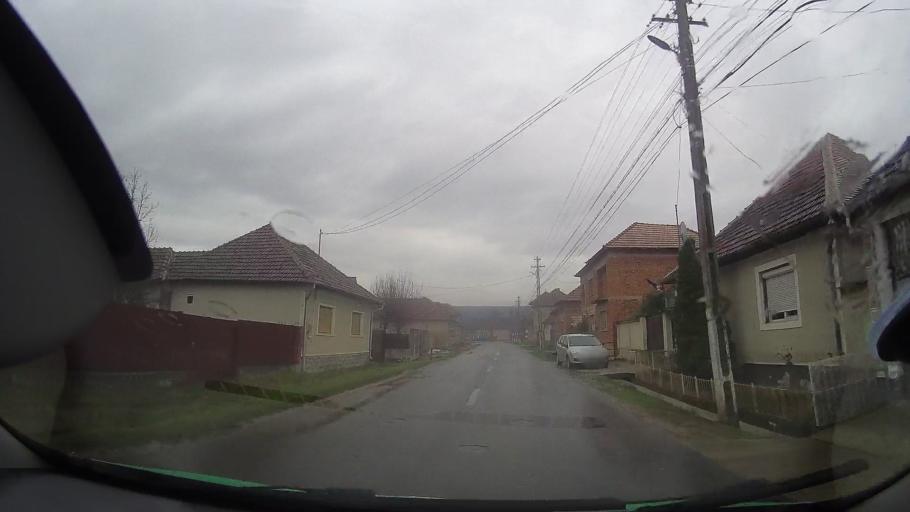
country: RO
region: Bihor
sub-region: Comuna Rabagani
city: Rabagani
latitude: 46.7470
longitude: 22.2347
